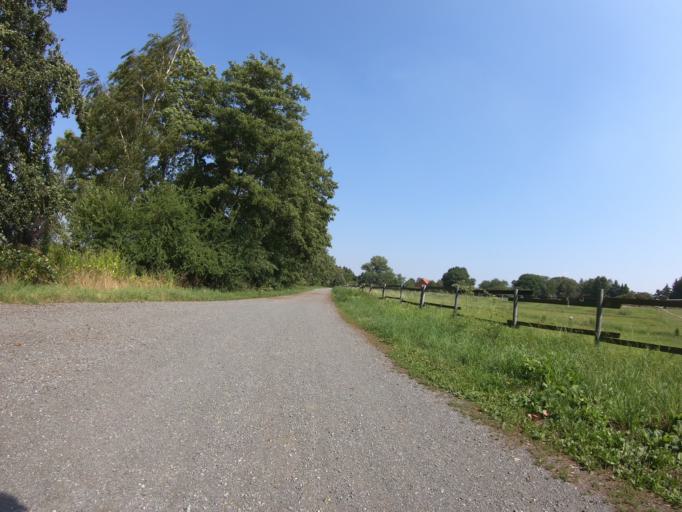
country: DE
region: Lower Saxony
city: Sickte
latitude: 52.2376
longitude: 10.5955
